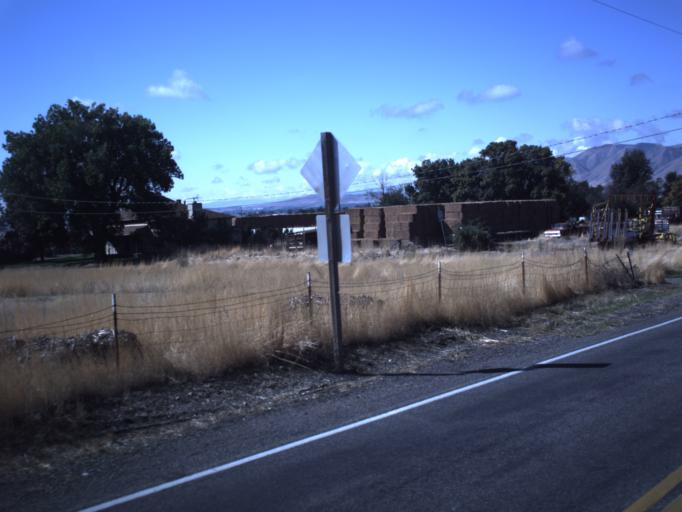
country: US
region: Utah
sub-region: Utah County
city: Spanish Fork
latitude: 40.0984
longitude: -111.6829
